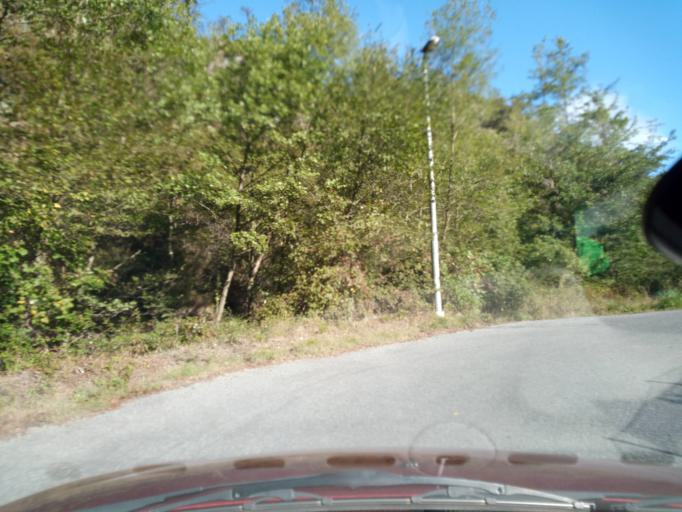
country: IT
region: Liguria
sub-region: Provincia di Genova
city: Isoverde
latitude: 44.4889
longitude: 8.8383
